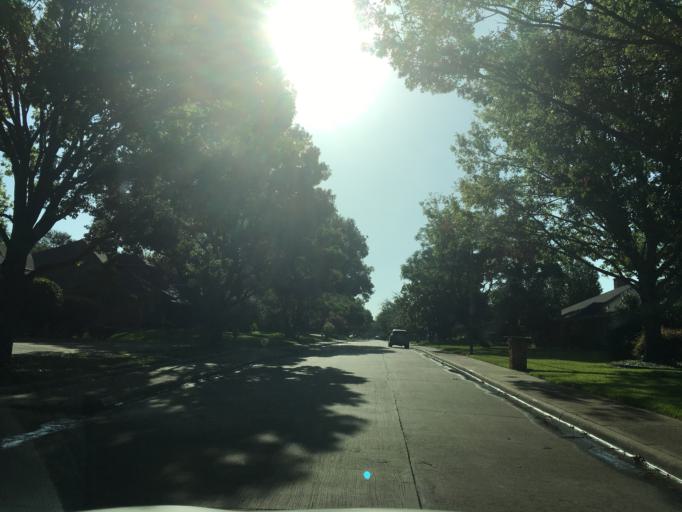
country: US
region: Texas
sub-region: Dallas County
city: Richardson
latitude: 32.8897
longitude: -96.7219
